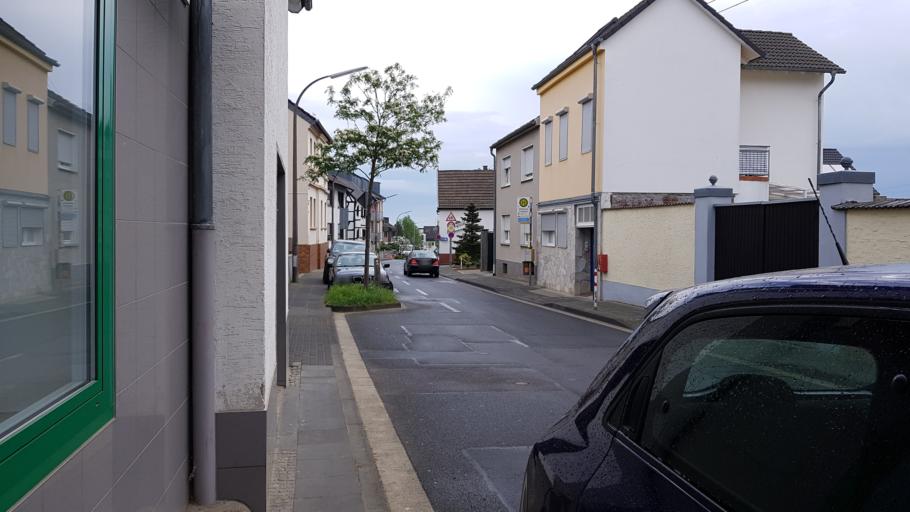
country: DE
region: North Rhine-Westphalia
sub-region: Regierungsbezirk Koln
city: Alfter
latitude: 50.7174
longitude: 7.0236
